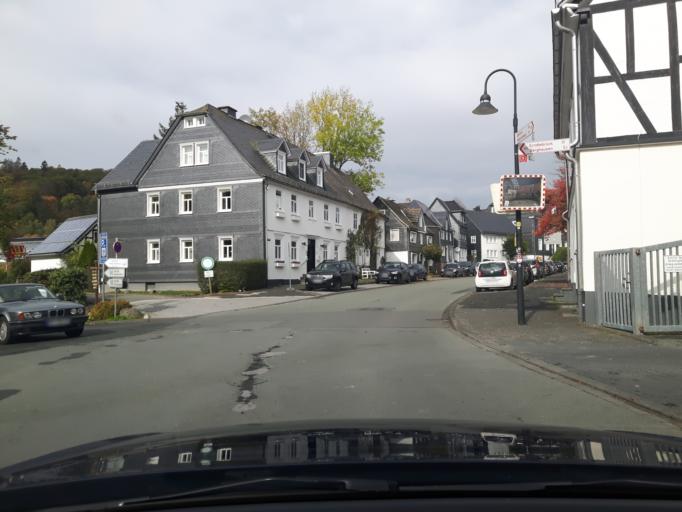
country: DE
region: North Rhine-Westphalia
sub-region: Regierungsbezirk Arnsberg
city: Bad Berleburg
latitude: 51.0527
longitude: 8.3886
